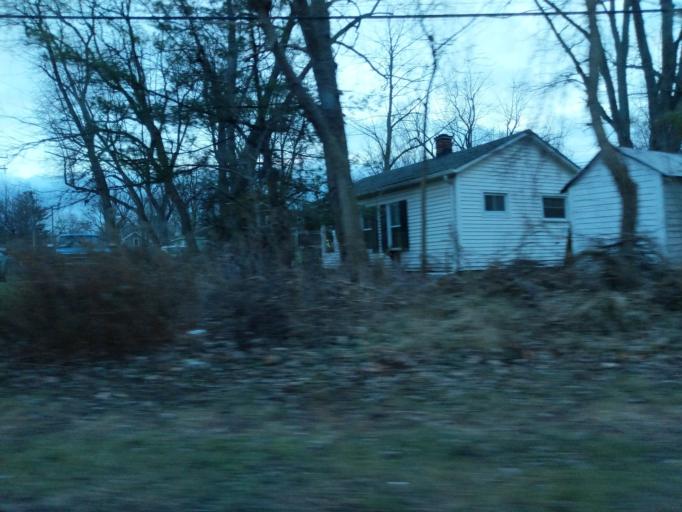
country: US
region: Michigan
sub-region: Lapeer County
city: Almont
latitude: 42.9265
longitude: -83.0465
